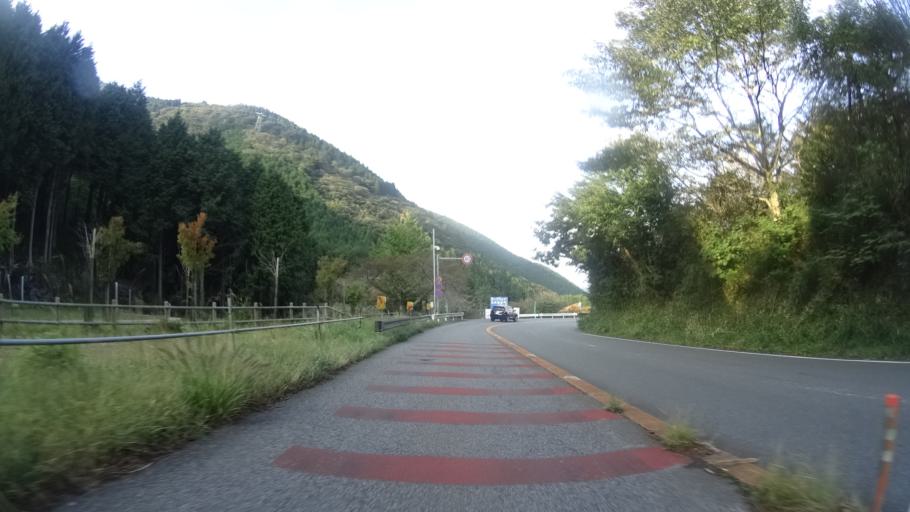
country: JP
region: Oita
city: Beppu
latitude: 33.2763
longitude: 131.4456
